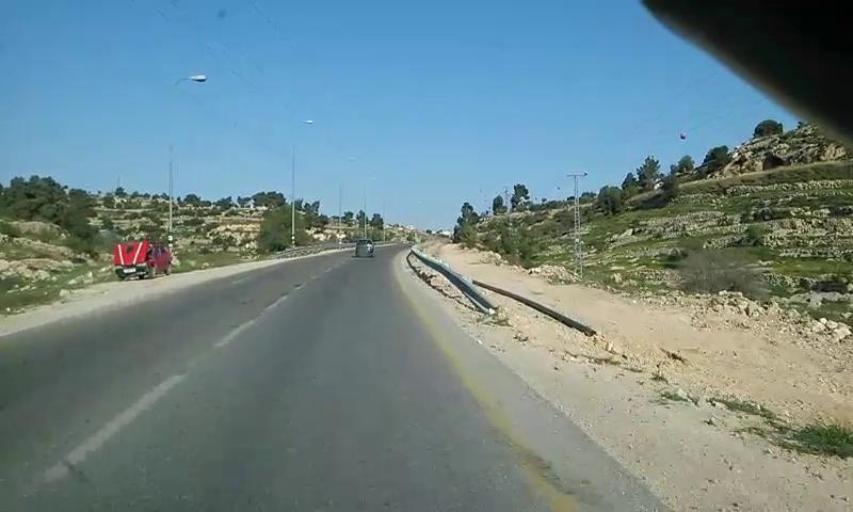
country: PS
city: Khallat ad Dar
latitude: 31.5048
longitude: 35.1292
